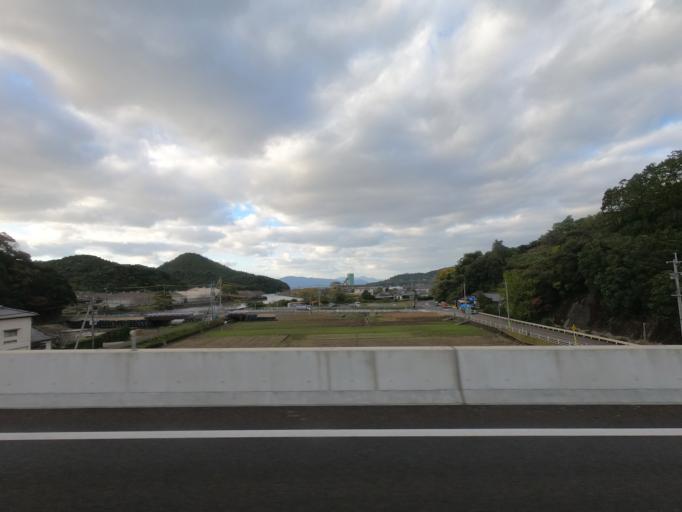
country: JP
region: Kumamoto
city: Minamata
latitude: 32.2267
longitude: 130.4363
